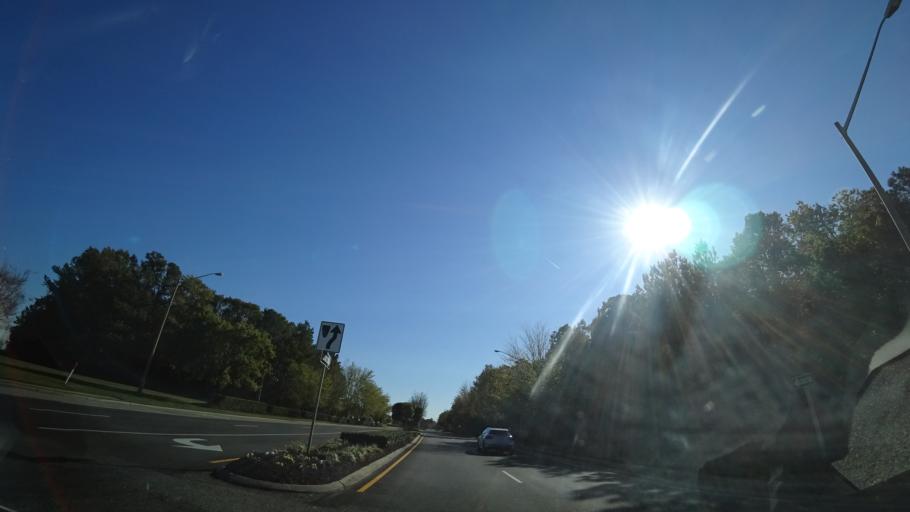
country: US
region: Virginia
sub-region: City of Newport News
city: Newport News
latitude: 36.8905
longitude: -76.4377
